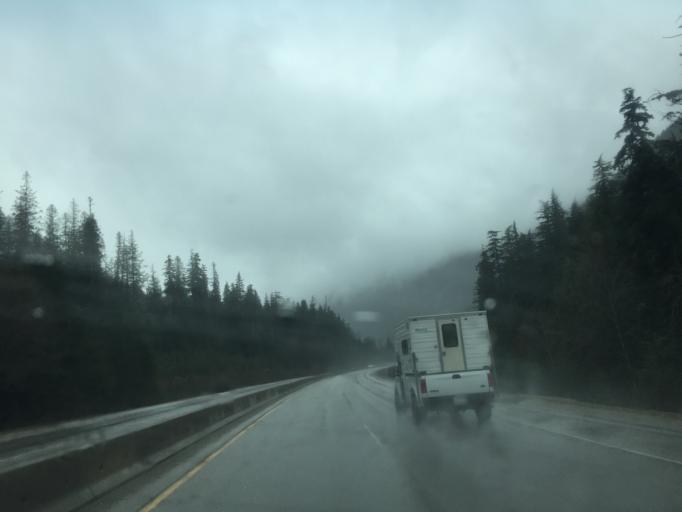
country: CA
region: British Columbia
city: Hope
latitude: 49.5434
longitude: -121.1965
